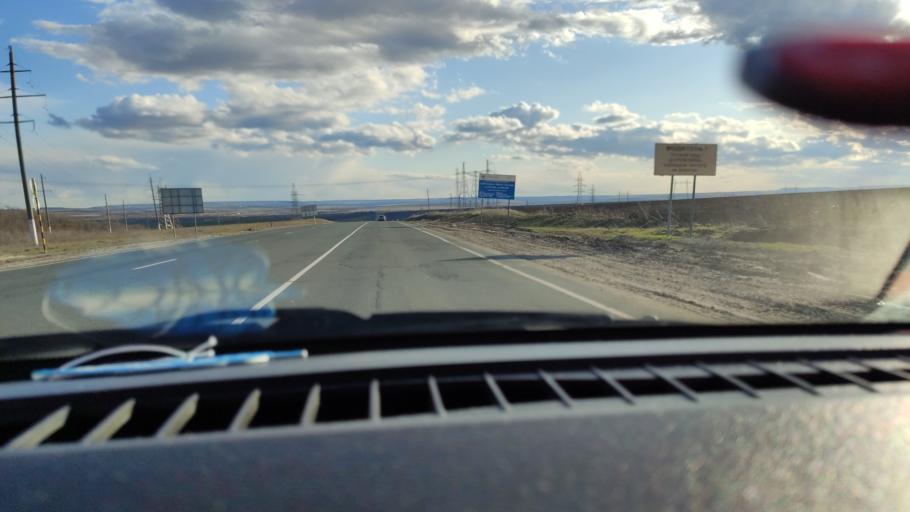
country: RU
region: Saratov
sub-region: Saratovskiy Rayon
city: Saratov
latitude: 51.7661
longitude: 46.0773
